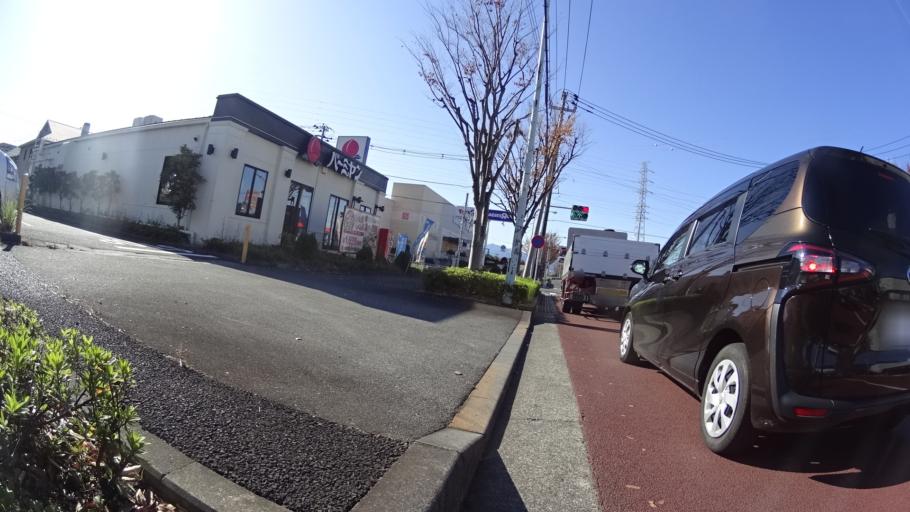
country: JP
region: Tokyo
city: Hino
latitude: 35.5995
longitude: 139.3821
